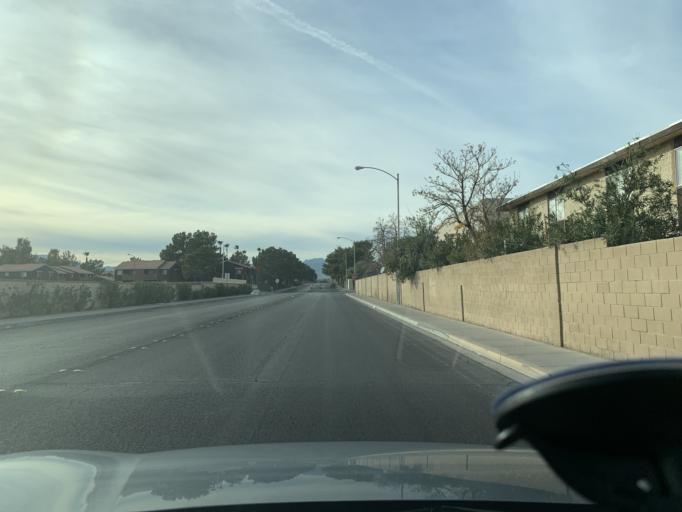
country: US
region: Nevada
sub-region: Clark County
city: Spring Valley
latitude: 36.1114
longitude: -115.2152
